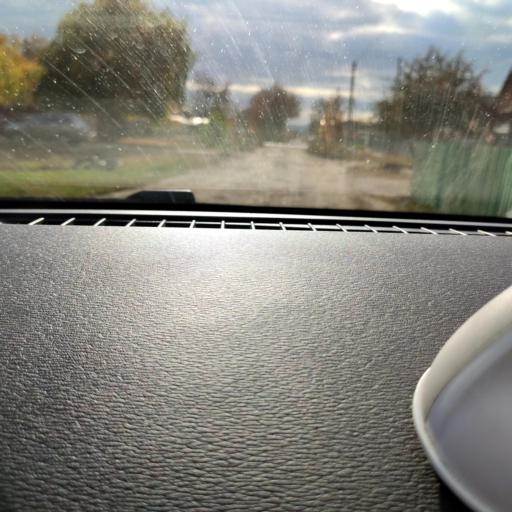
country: RU
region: Samara
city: Petra-Dubrava
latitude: 53.2468
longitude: 50.3140
